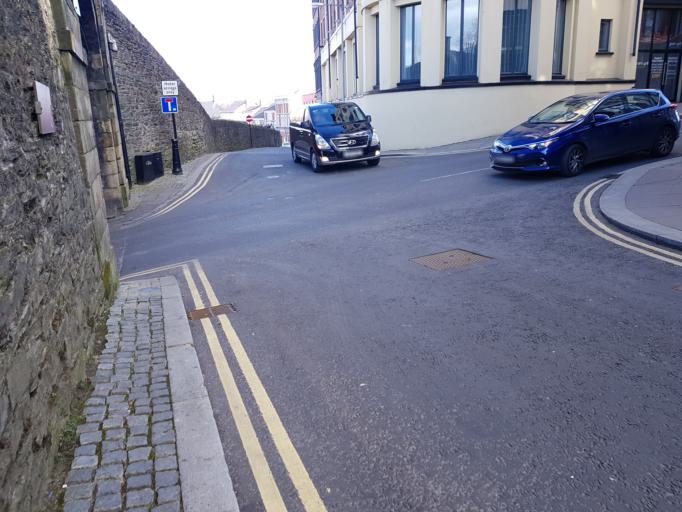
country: GB
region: Northern Ireland
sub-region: City of Derry
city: Derry
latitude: 54.9961
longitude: -7.3233
